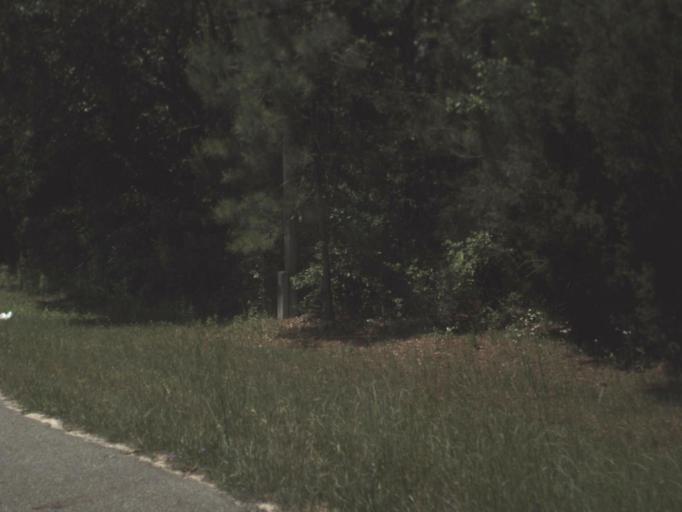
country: US
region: Florida
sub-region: Jackson County
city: Marianna
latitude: 30.7430
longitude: -85.2301
